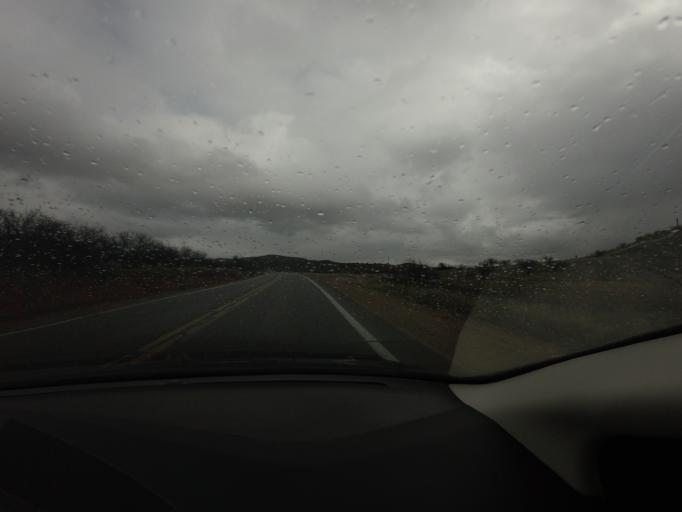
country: US
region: Arizona
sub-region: Yavapai County
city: Cornville
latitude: 34.7091
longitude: -111.8780
